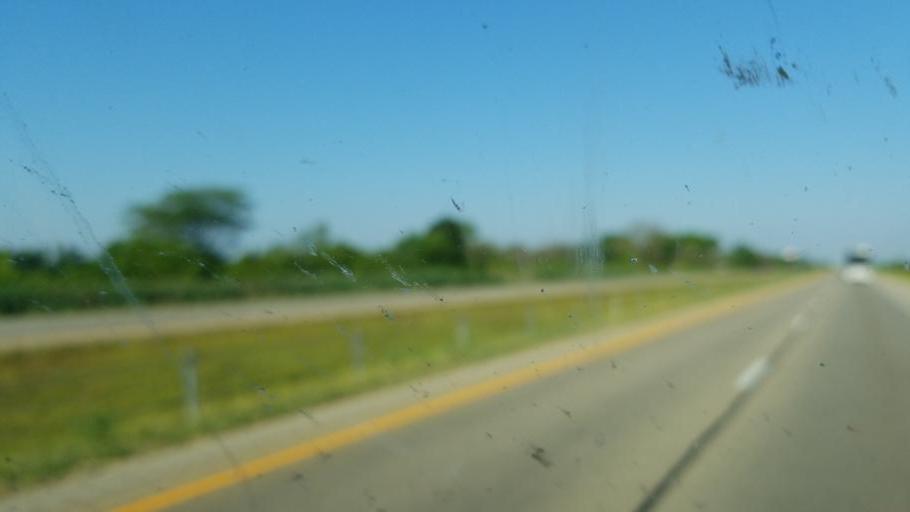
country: US
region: Illinois
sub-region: LaSalle County
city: Ottawa
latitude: 41.3686
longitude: -88.8763
